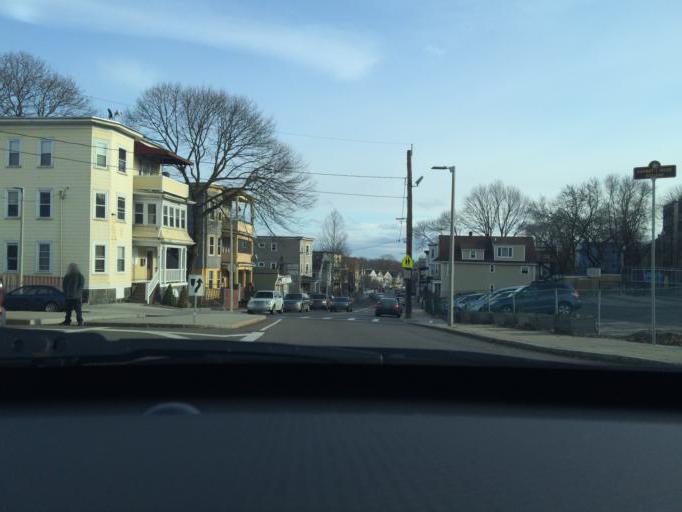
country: US
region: Massachusetts
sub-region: Suffolk County
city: Jamaica Plain
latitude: 42.3018
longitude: -71.0856
